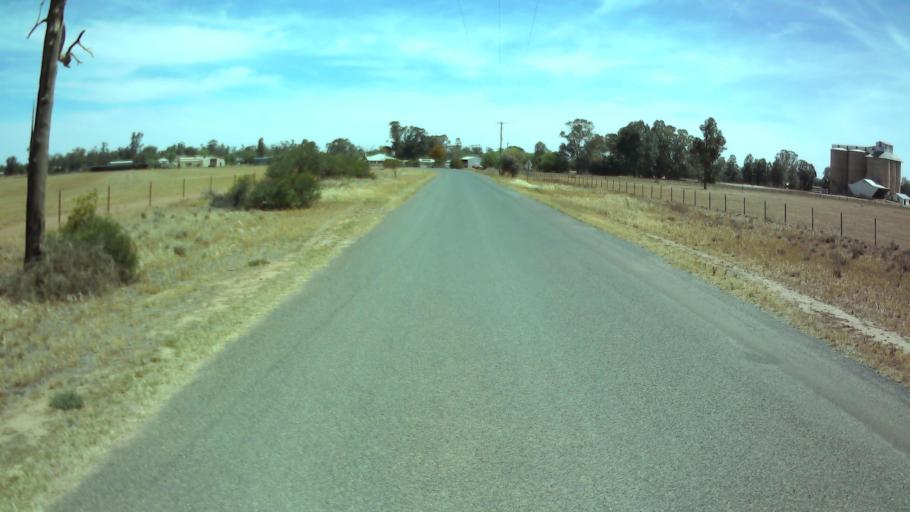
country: AU
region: New South Wales
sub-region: Weddin
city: Grenfell
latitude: -33.8376
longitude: 147.7460
